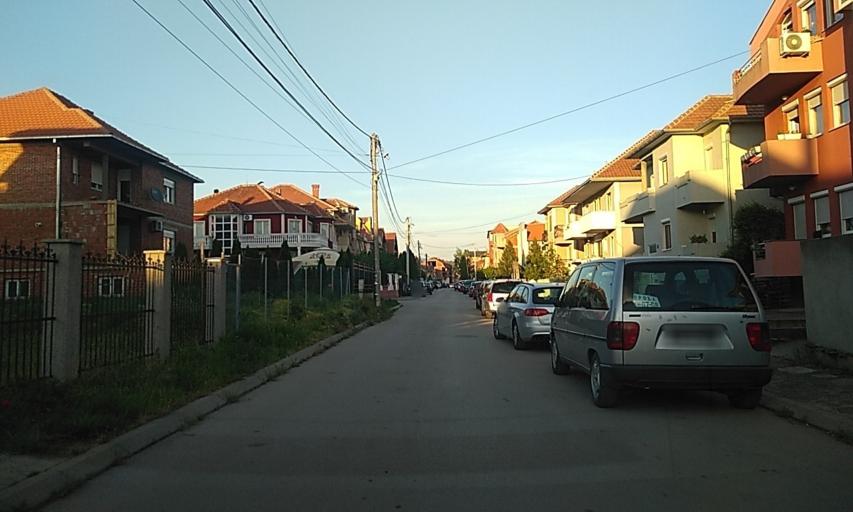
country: RS
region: Central Serbia
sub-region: Nisavski Okrug
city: Nis
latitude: 43.3348
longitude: 21.9309
